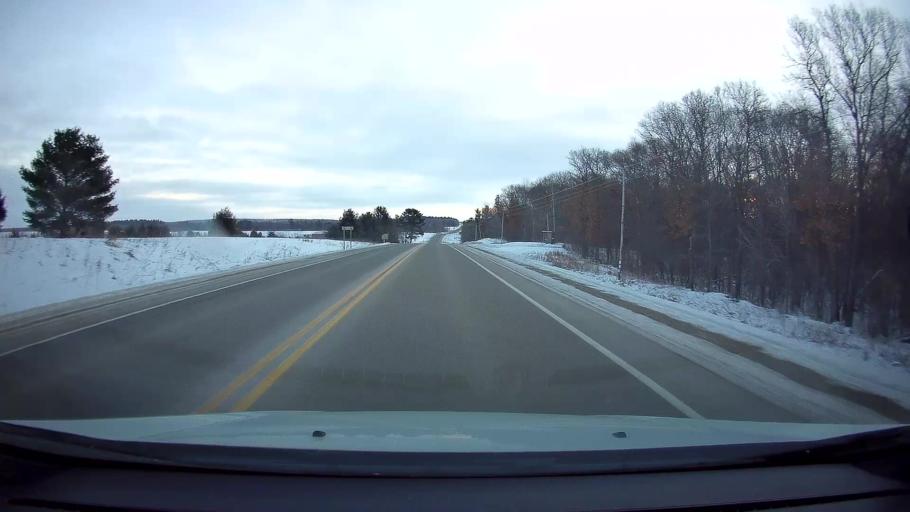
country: US
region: Wisconsin
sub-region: Saint Croix County
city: New Richmond
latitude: 45.1371
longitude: -92.4242
